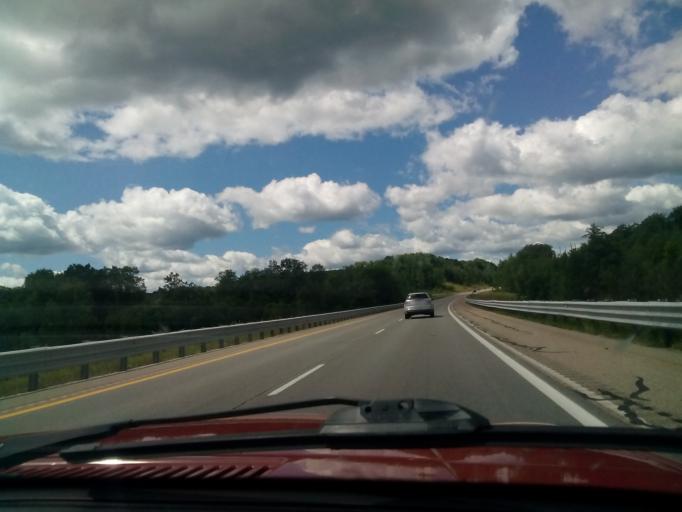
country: US
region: Michigan
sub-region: Ogemaw County
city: West Branch
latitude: 44.2619
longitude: -84.2617
